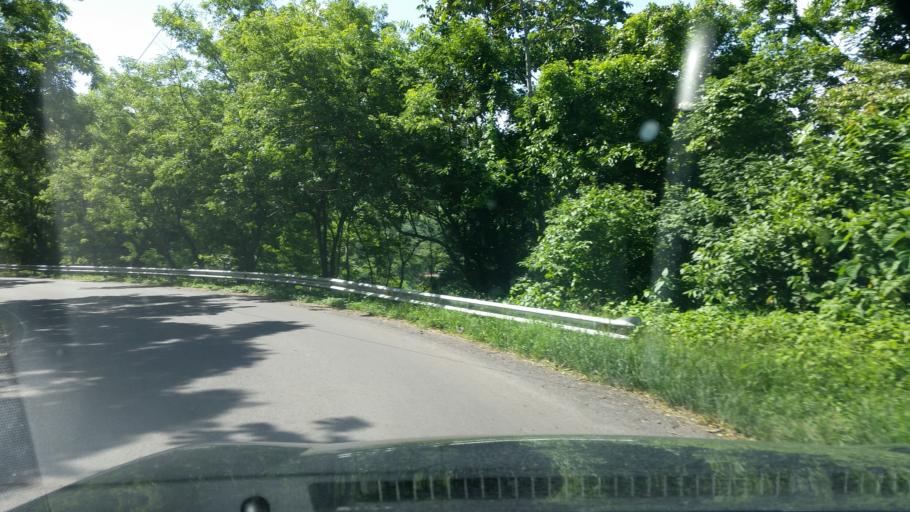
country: NI
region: Matagalpa
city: San Ramon
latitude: 13.0146
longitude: -85.7889
